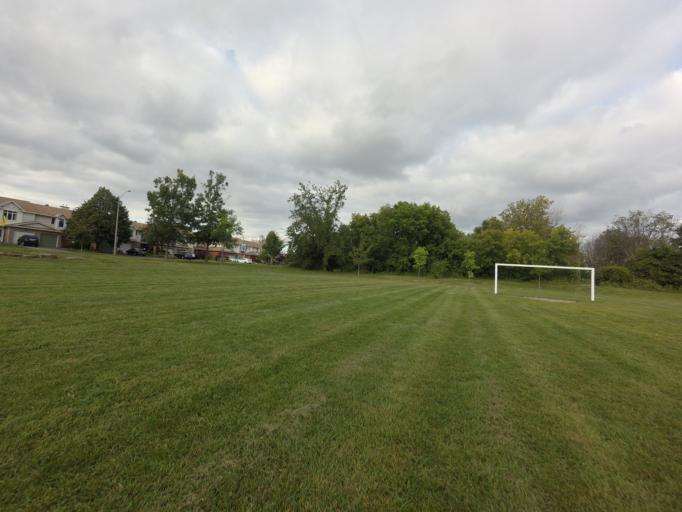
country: CA
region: Ontario
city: Bells Corners
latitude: 45.2827
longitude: -75.7298
